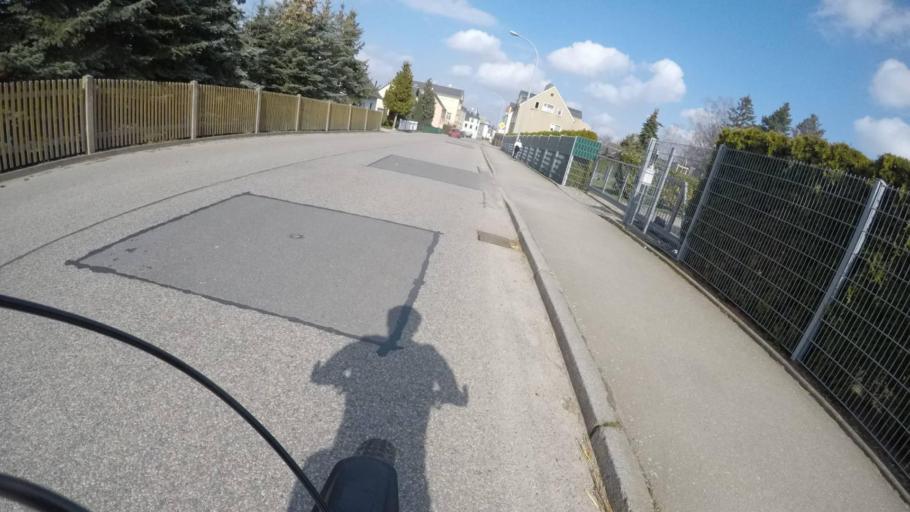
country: DE
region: Saxony
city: Limbach-Oberfrohna
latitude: 50.8492
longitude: 12.7312
